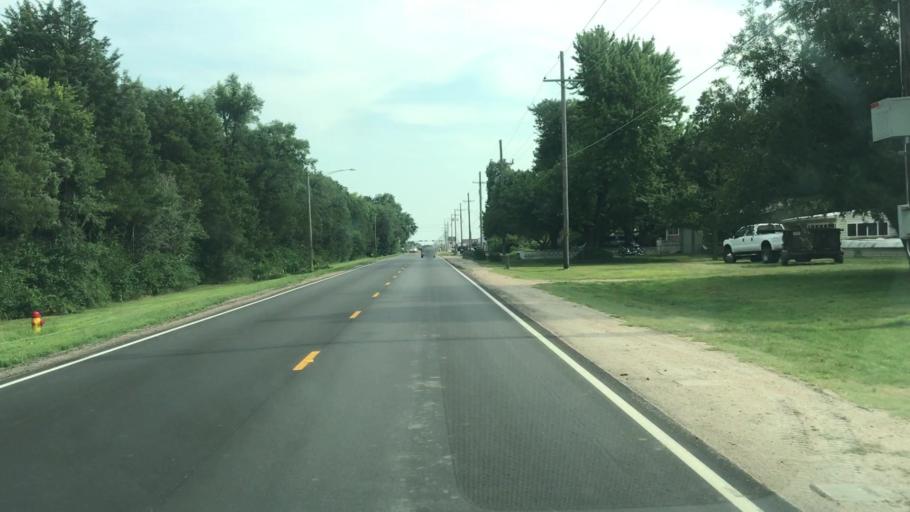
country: US
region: Nebraska
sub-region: Hall County
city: Grand Island
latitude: 40.9498
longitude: -98.3788
